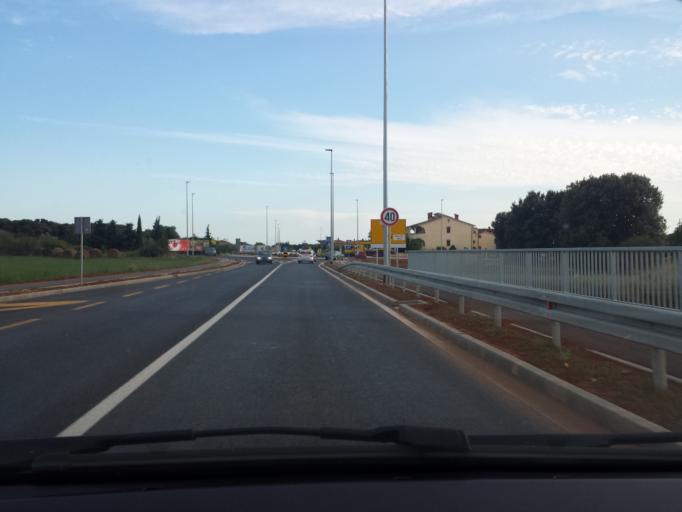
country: HR
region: Istarska
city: Galizana
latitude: 44.9050
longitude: 13.8465
